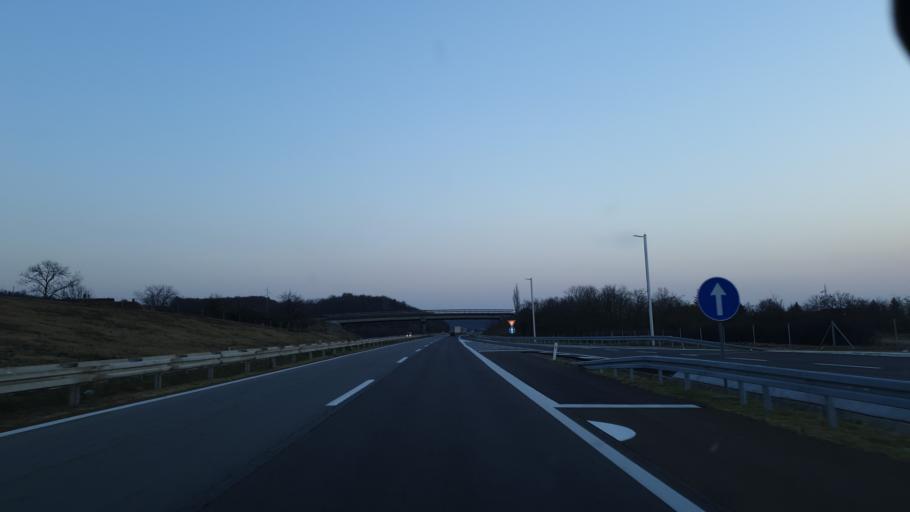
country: RS
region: Central Serbia
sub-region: Pomoravski Okrug
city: Paracin
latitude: 43.7958
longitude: 21.4340
